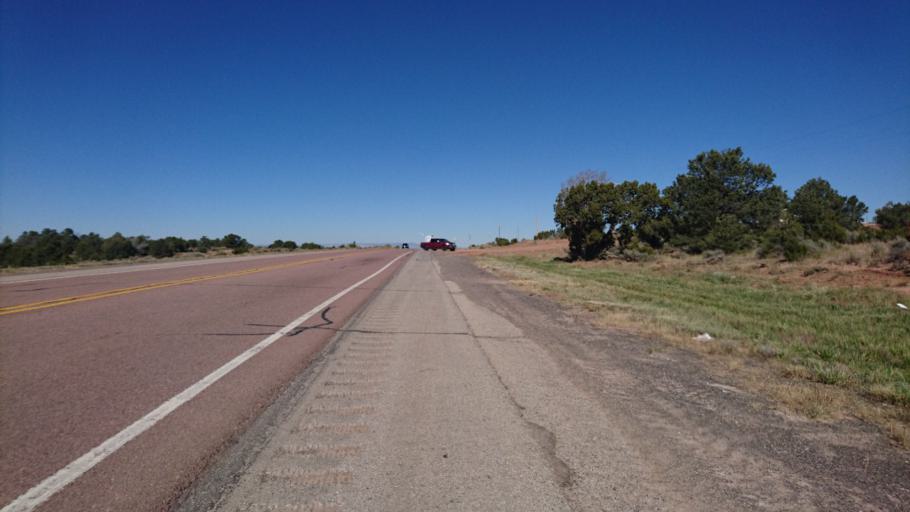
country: US
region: New Mexico
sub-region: McKinley County
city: Gallup
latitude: 35.3821
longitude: -108.7535
